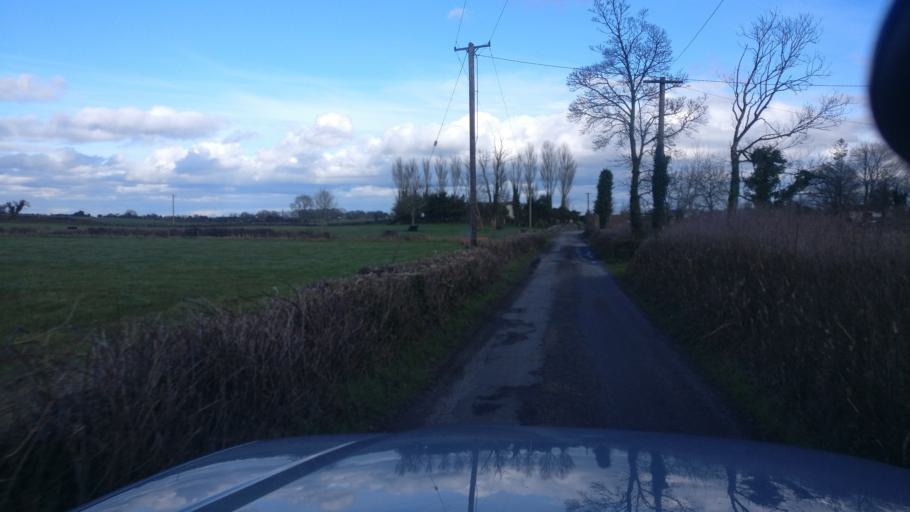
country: IE
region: Connaught
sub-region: County Galway
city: Loughrea
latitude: 53.2160
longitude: -8.4141
